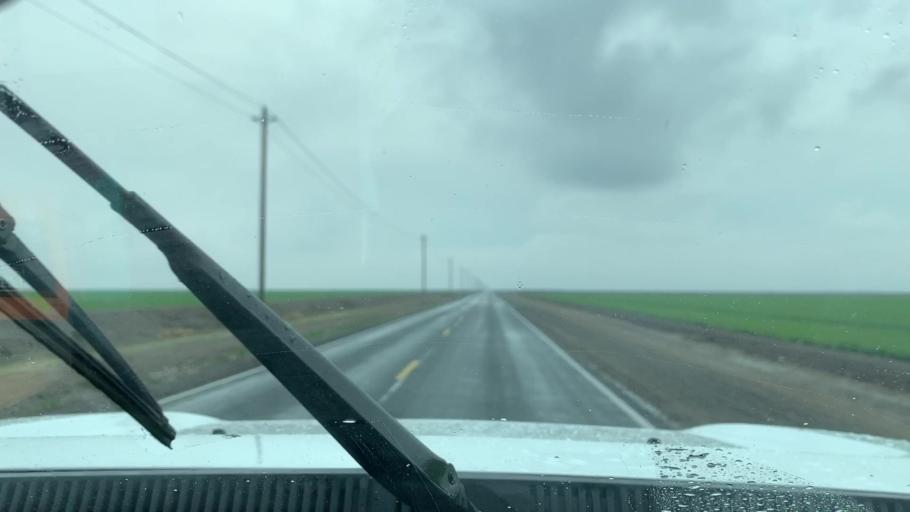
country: US
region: California
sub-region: Kings County
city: Corcoran
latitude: 35.9883
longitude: -119.5720
